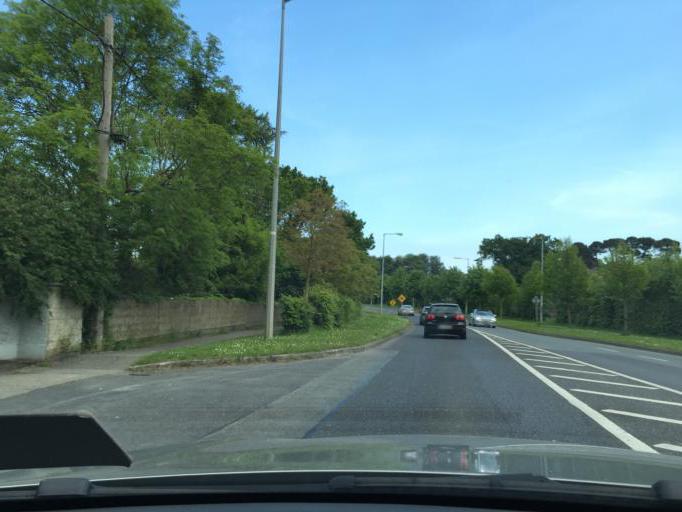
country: IE
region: Leinster
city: Ballyboden
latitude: 53.2792
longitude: -6.3128
